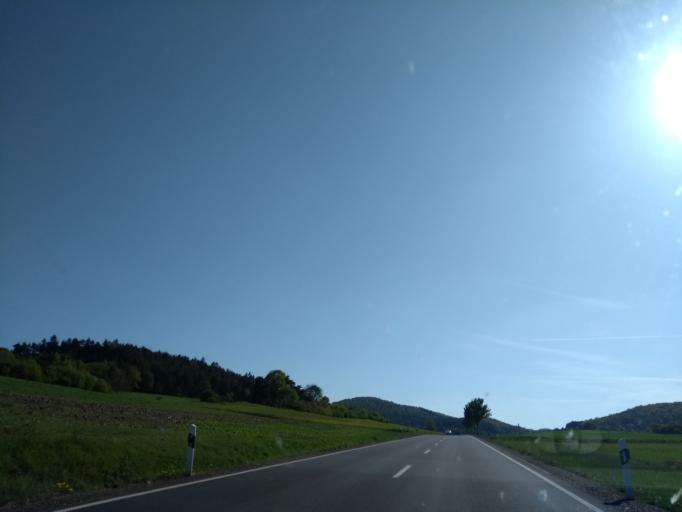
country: DE
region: Hesse
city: Battenberg
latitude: 50.9831
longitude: 8.6176
